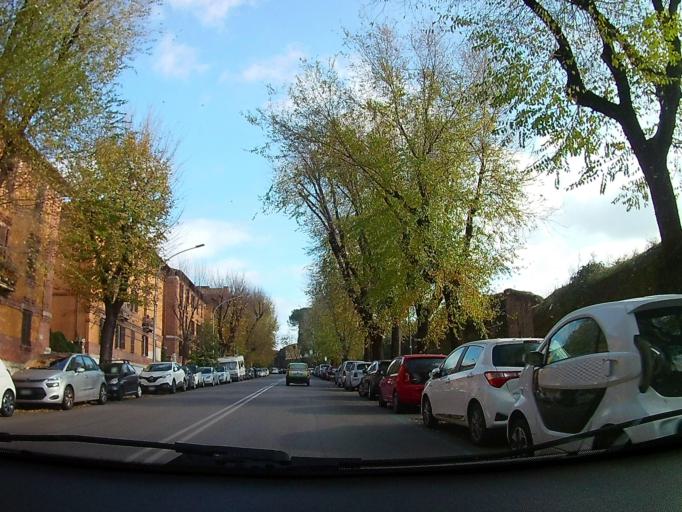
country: IT
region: Latium
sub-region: Citta metropolitana di Roma Capitale
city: Rome
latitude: 41.8771
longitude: 12.4837
